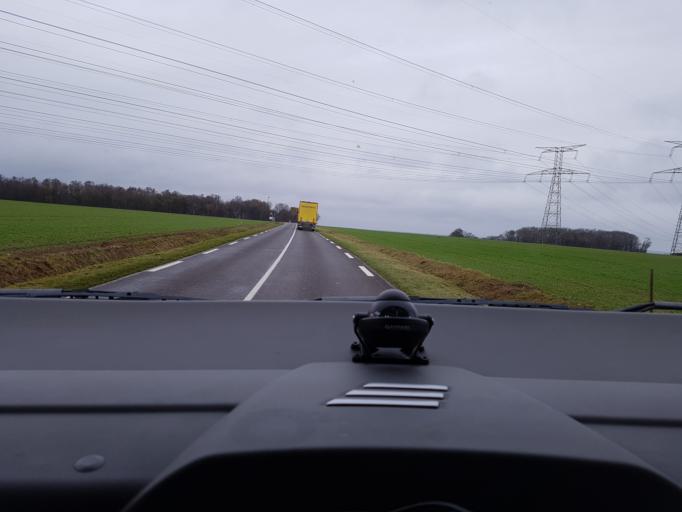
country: FR
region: Haute-Normandie
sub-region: Departement de la Seine-Maritime
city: Gournay-en-Bray
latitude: 49.4520
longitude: 1.6746
